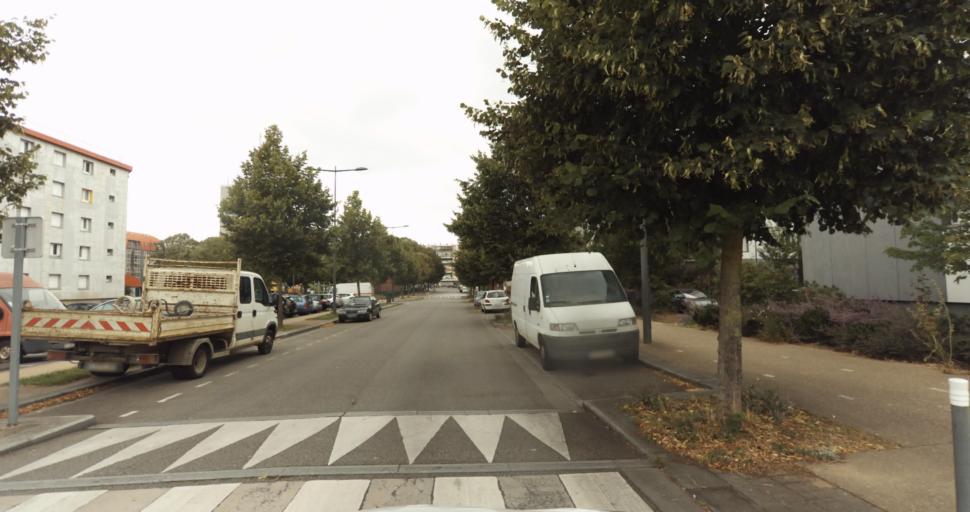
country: FR
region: Haute-Normandie
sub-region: Departement de l'Eure
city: Evreux
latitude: 49.0075
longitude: 1.1617
